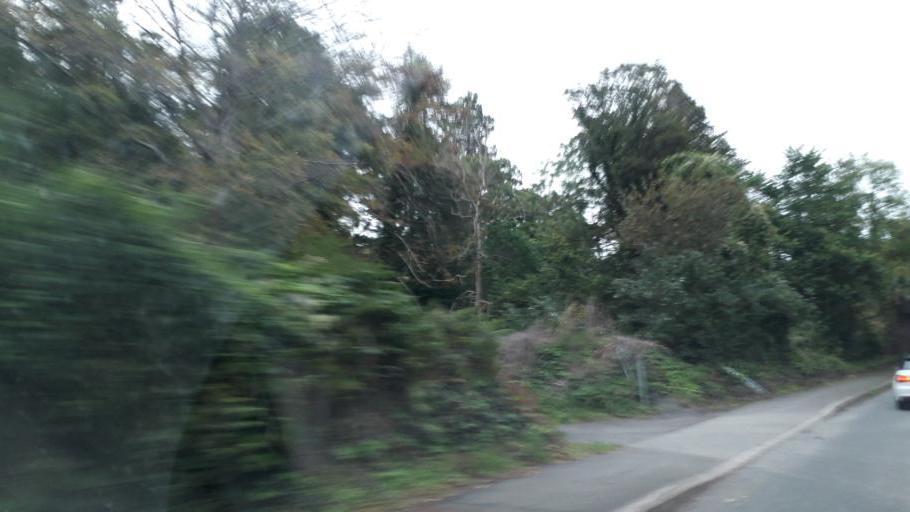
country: IE
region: Leinster
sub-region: Wicklow
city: Enniskerry
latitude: 53.1905
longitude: -6.1545
